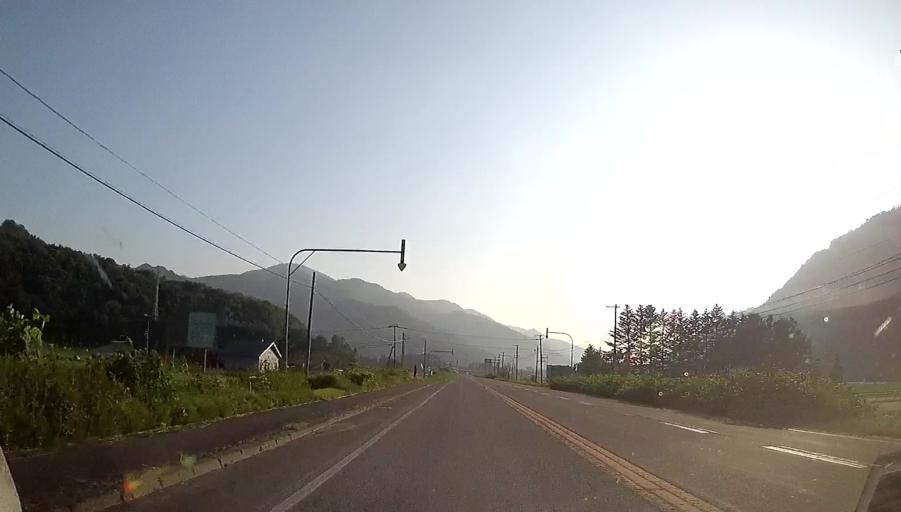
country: JP
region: Hokkaido
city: Shimo-furano
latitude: 42.8933
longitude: 142.5480
